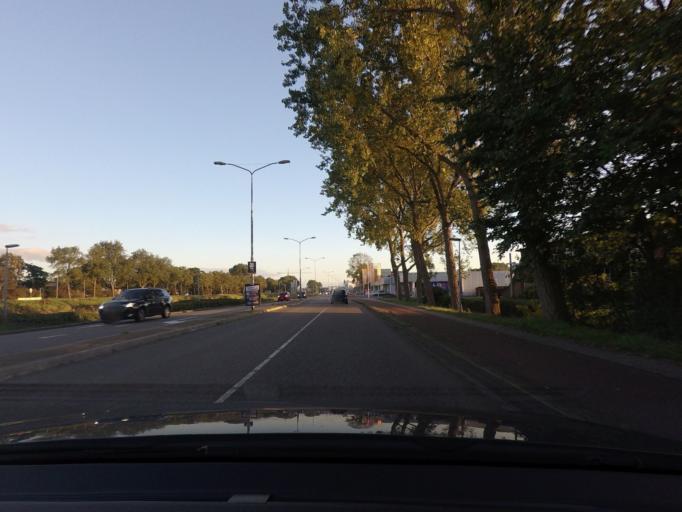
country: NL
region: North Holland
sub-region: Gemeente Alkmaar
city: Alkmaar
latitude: 52.6445
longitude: 4.7439
